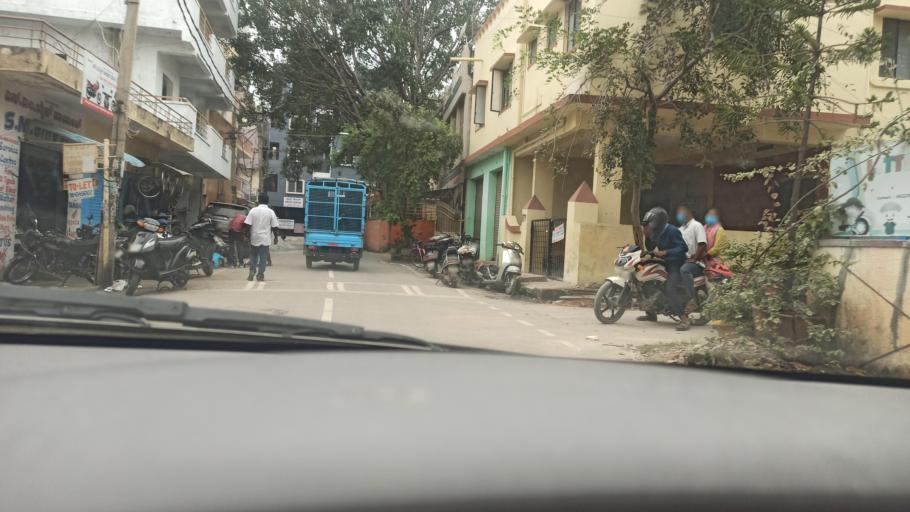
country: IN
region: Karnataka
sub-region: Bangalore Urban
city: Bangalore
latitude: 12.9893
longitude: 77.6845
